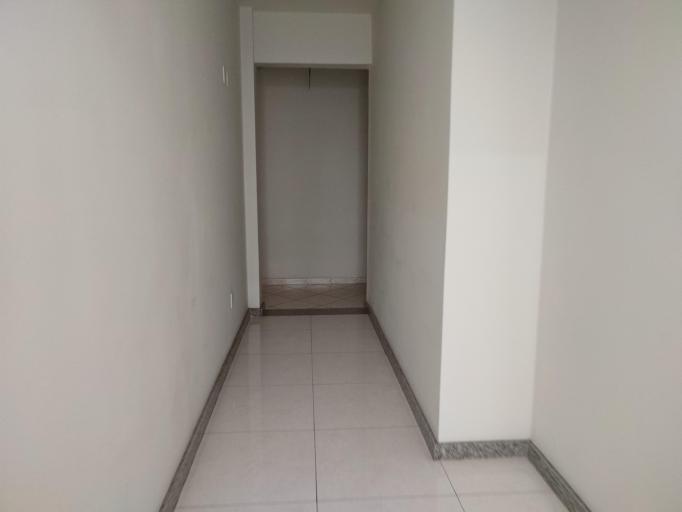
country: BR
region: Bahia
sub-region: Mutuipe
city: Mutuipe
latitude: -13.2285
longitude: -39.5034
